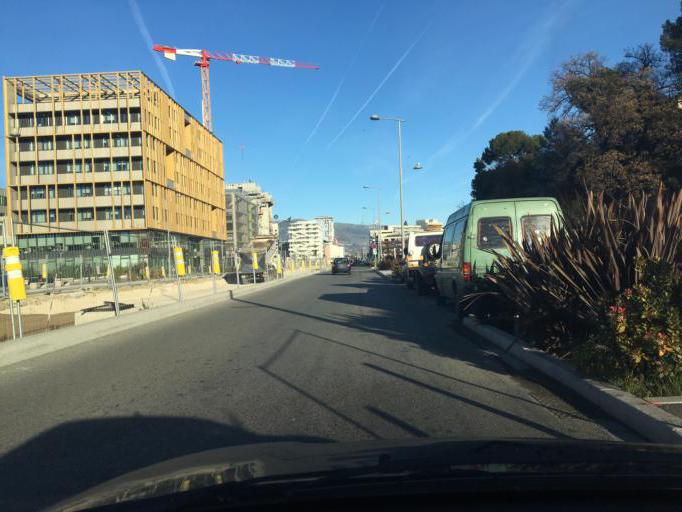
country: FR
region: Provence-Alpes-Cote d'Azur
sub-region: Departement des Alpes-Maritimes
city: Saint-Laurent-du-Var
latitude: 43.6788
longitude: 7.2050
